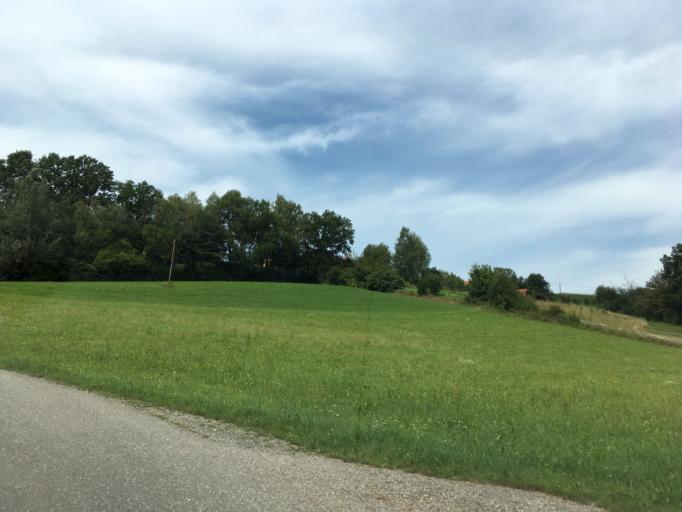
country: AT
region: Styria
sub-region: Politischer Bezirk Deutschlandsberg
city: Wettmannstatten
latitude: 46.7953
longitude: 15.4020
